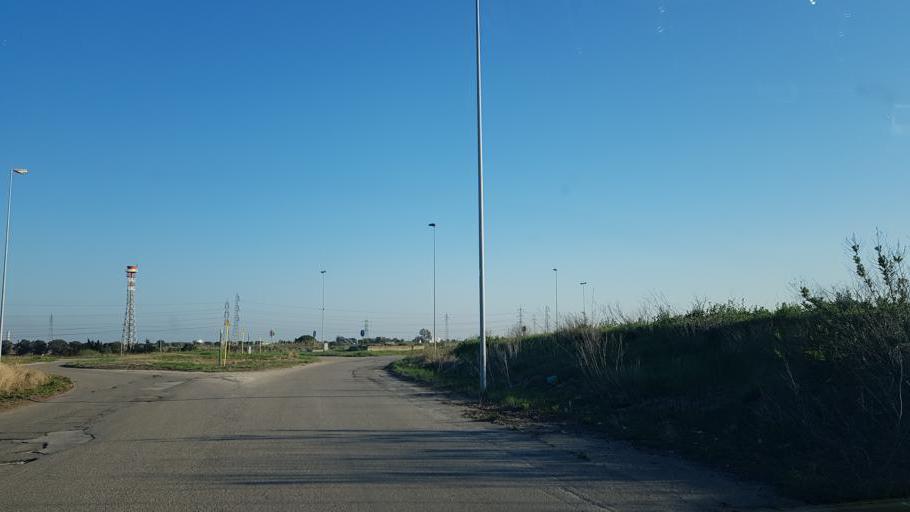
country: IT
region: Apulia
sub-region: Provincia di Brindisi
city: La Rosa
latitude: 40.6190
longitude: 17.9713
